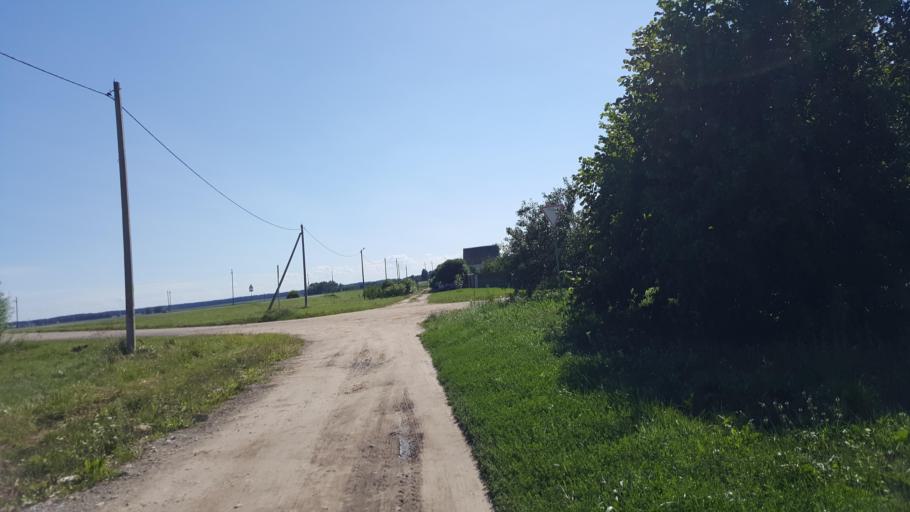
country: BY
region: Brest
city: Charnawchytsy
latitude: 52.2068
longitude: 23.7419
